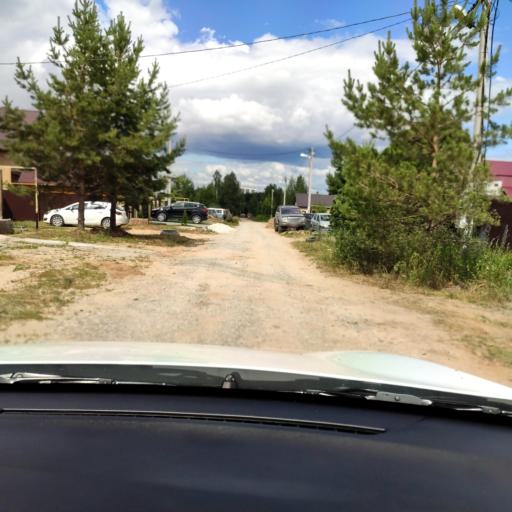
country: RU
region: Tatarstan
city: Vysokaya Gora
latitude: 55.7832
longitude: 49.2709
